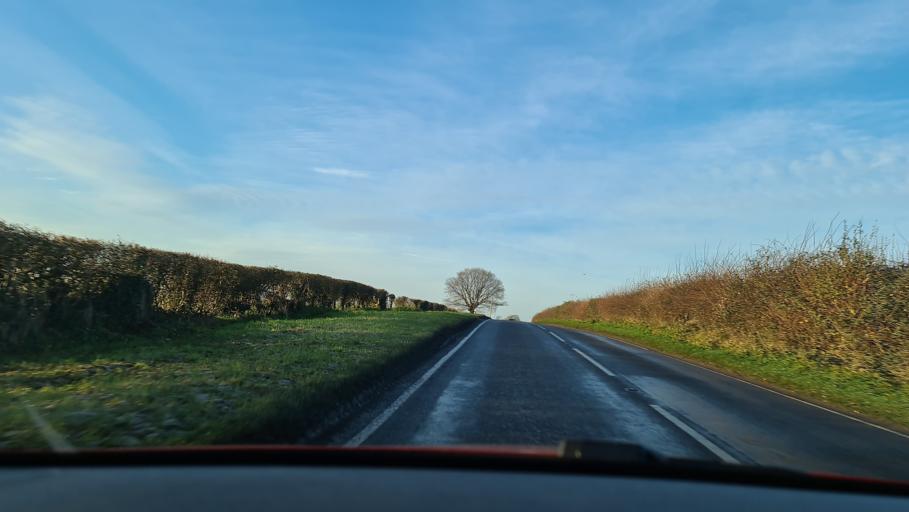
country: GB
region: England
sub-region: Buckinghamshire
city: Haddenham
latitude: 51.8108
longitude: -0.9398
